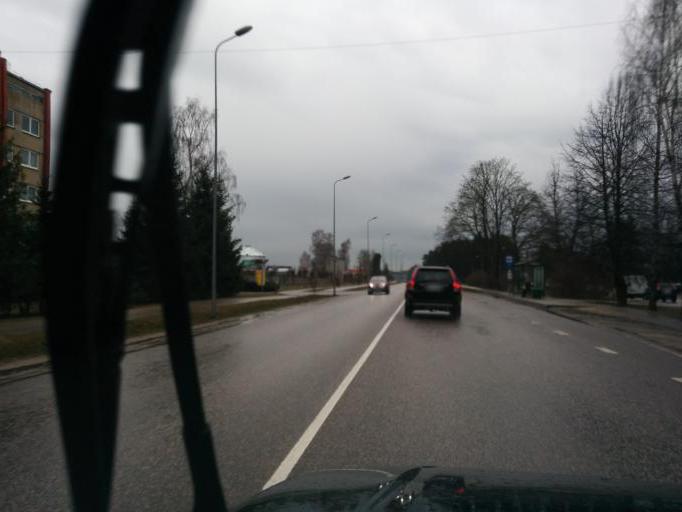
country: LV
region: Kekava
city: Balozi
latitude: 56.9016
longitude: 24.1467
